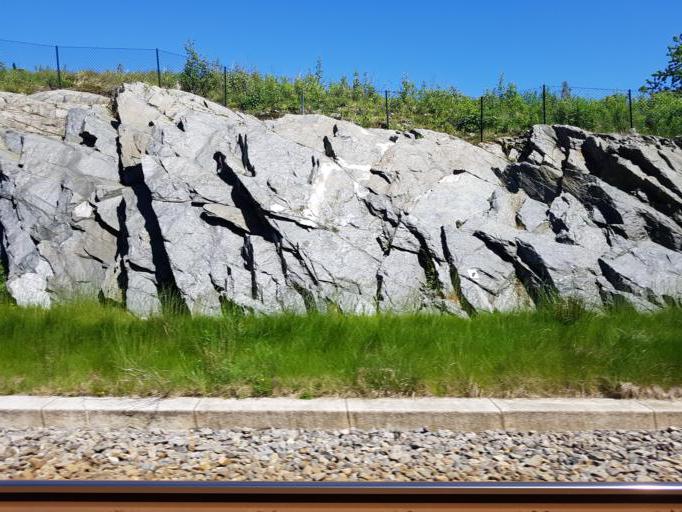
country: NO
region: Hordaland
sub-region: Bergen
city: Ytrebygda
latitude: 60.2889
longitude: 5.2556
